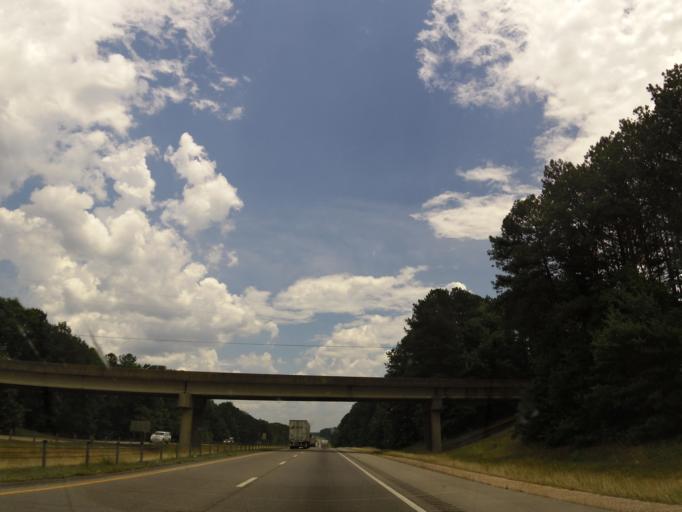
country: US
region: Alabama
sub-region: Sumter County
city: York
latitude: 32.4450
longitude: -88.4159
